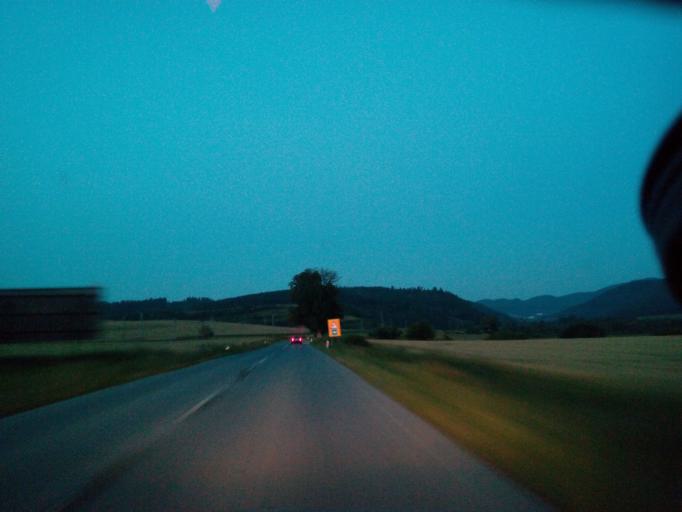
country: SK
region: Kosicky
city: Krompachy
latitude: 48.9458
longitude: 20.8098
